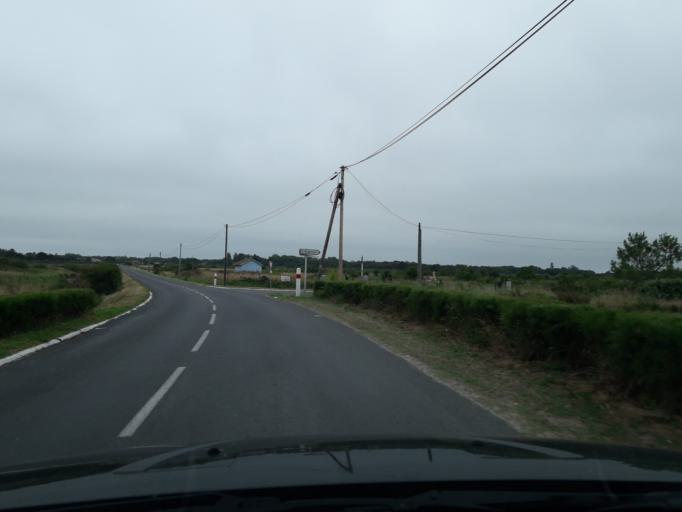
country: FR
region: Poitou-Charentes
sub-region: Departement de la Charente-Maritime
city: Boyard-Ville
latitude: 45.9608
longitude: -1.2491
